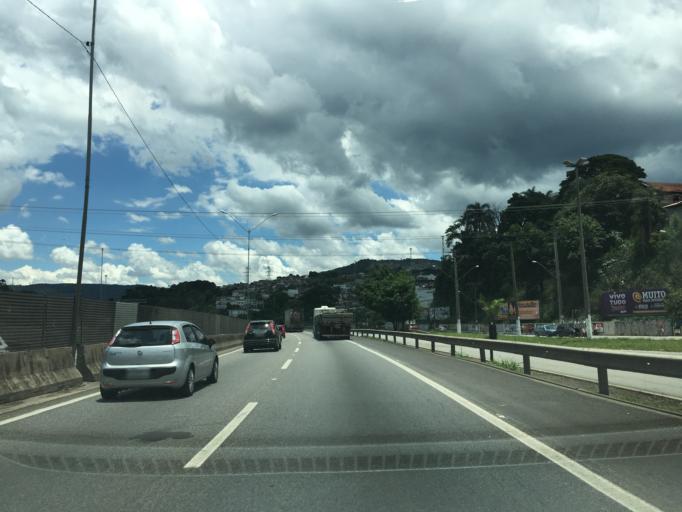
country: BR
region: Sao Paulo
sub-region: Mairipora
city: Mairipora
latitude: -23.3190
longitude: -46.5826
